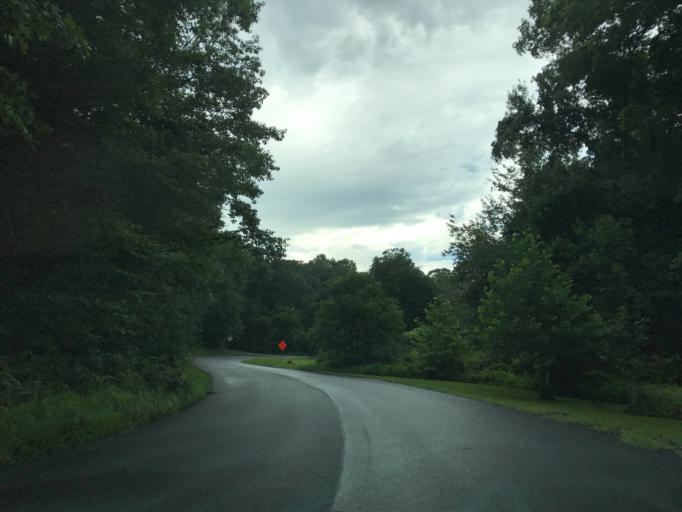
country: US
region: Pennsylvania
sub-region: York County
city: New Freedom
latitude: 39.6809
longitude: -76.7745
